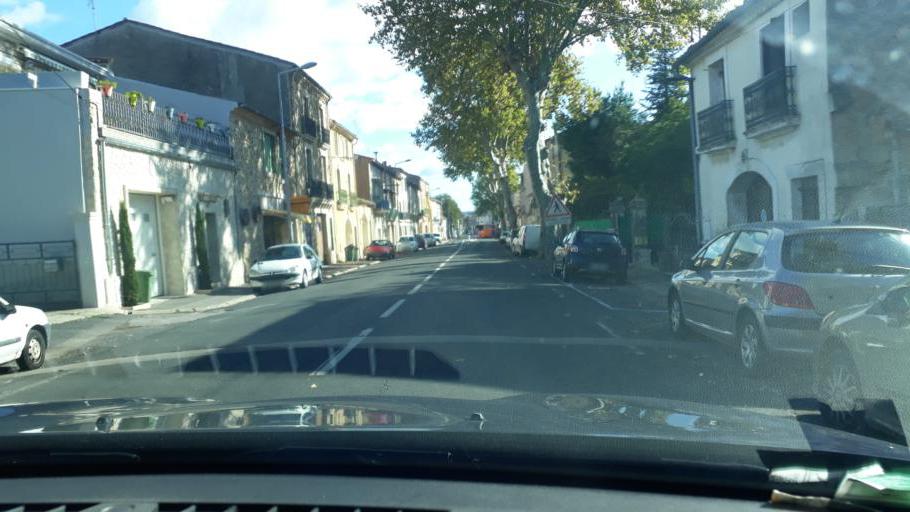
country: FR
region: Languedoc-Roussillon
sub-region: Departement de l'Herault
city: Saint-Andre-de-Sangonis
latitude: 43.6508
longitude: 3.5005
